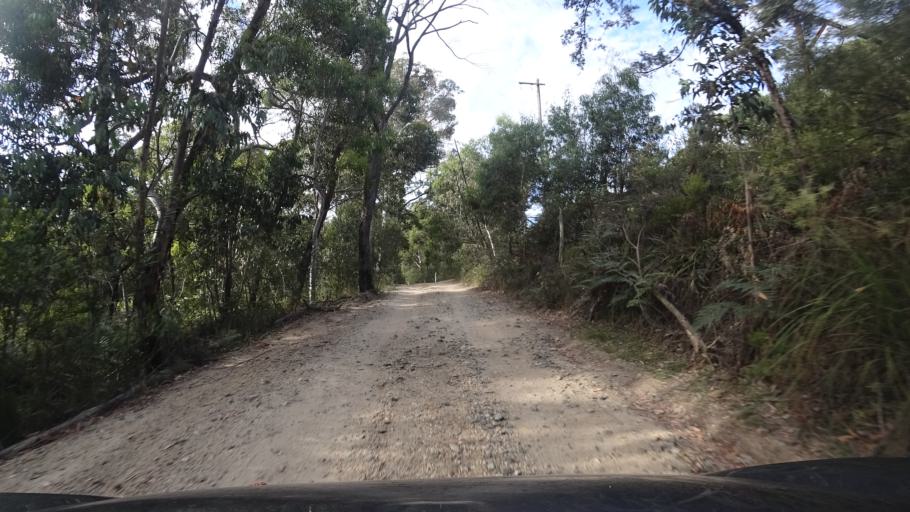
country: AU
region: New South Wales
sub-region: Lithgow
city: Lithgow
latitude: -33.4818
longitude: 150.2461
